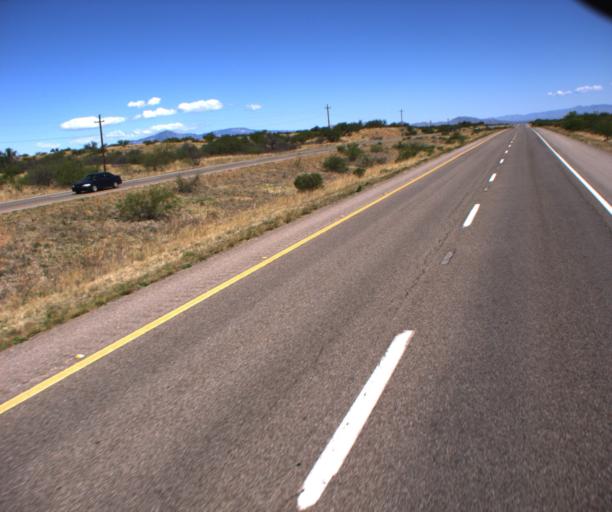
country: US
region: Arizona
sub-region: Cochise County
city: Whetstone
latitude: 31.8747
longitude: -110.3410
